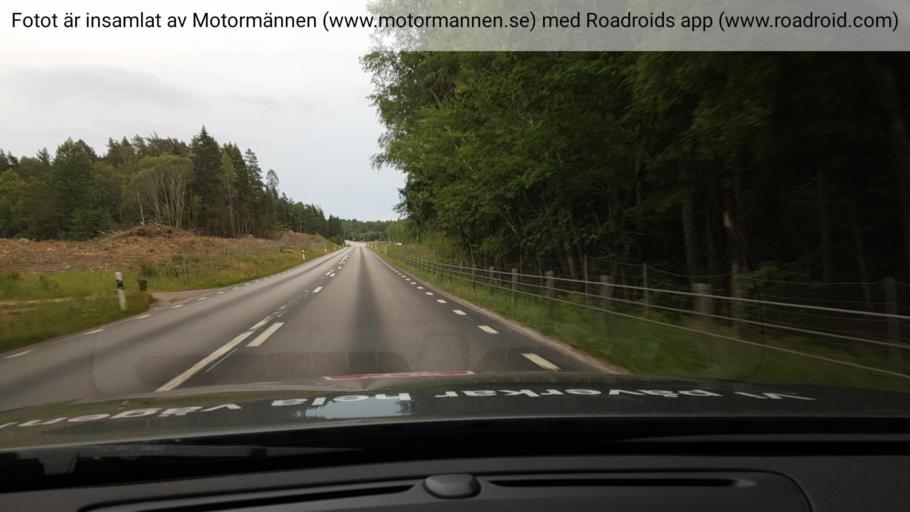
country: SE
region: OEstergoetland
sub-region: Motala Kommun
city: Borensberg
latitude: 58.5711
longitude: 15.2434
